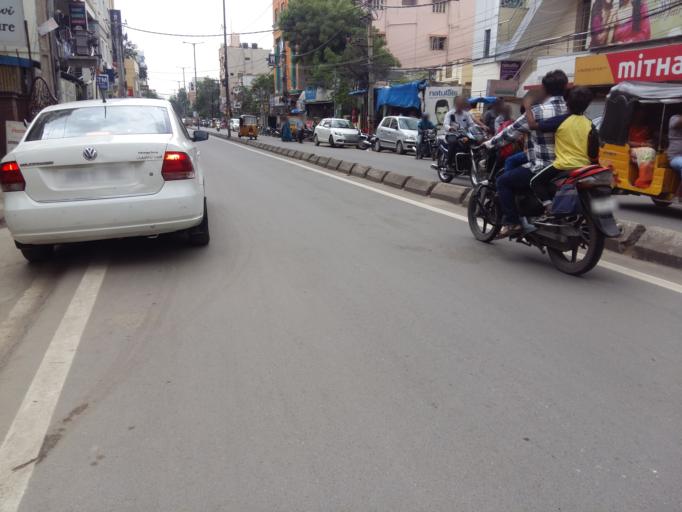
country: IN
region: Telangana
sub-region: Rangareddi
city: Kukatpalli
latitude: 17.4924
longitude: 78.4092
